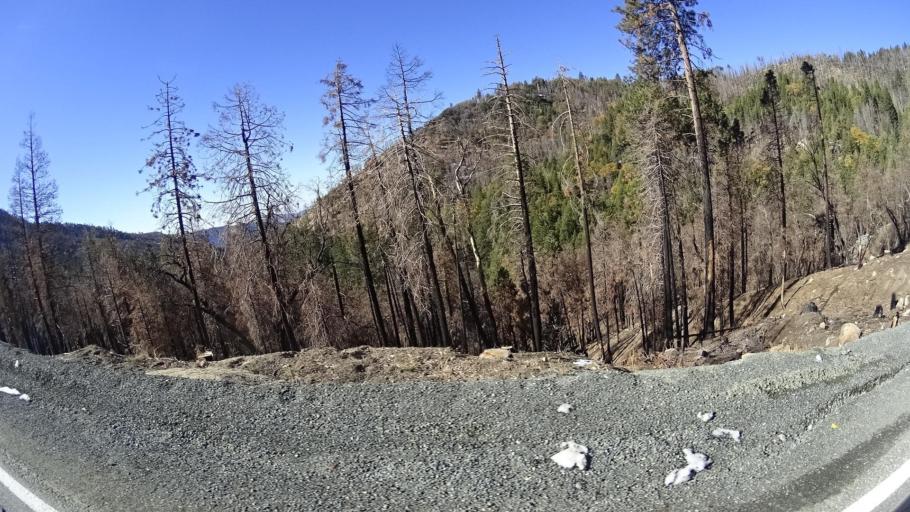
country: US
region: California
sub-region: Kern County
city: Alta Sierra
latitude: 35.7482
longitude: -118.5565
